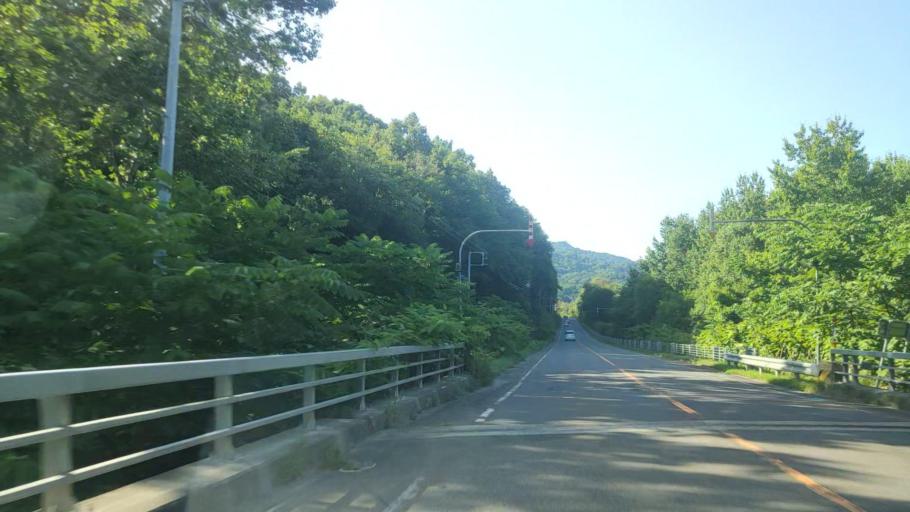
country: JP
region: Hokkaido
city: Nayoro
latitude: 44.7344
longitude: 142.1910
